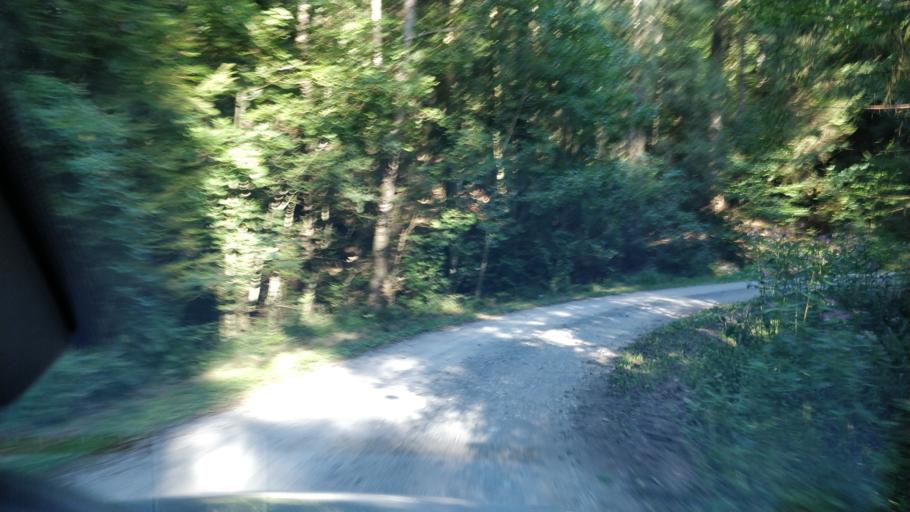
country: DE
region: Baden-Wuerttemberg
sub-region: Regierungsbezirk Stuttgart
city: Murrhardt
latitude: 49.0177
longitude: 9.5805
